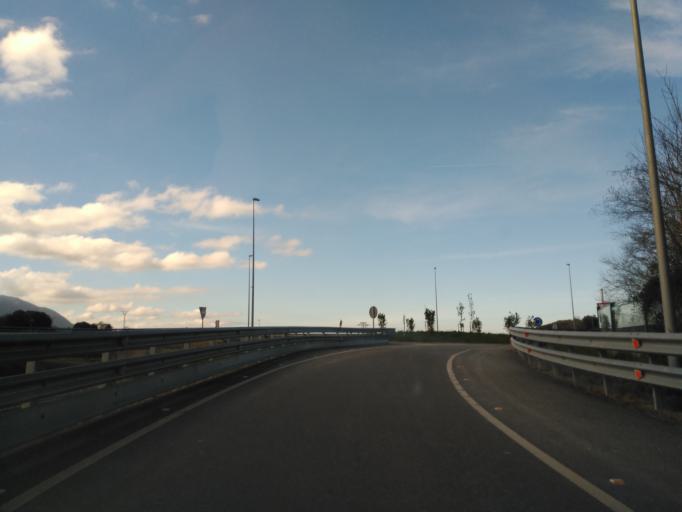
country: ES
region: Asturias
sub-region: Province of Asturias
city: Llanes
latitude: 43.4052
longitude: -4.7591
